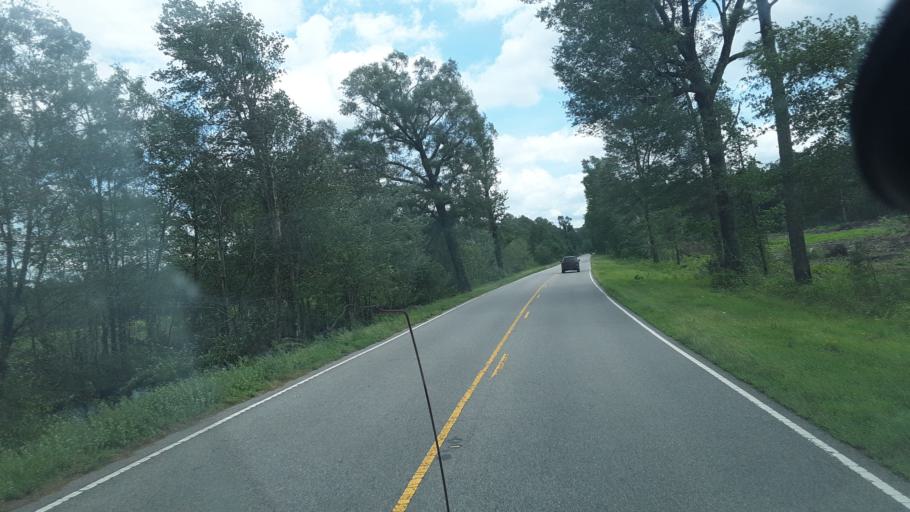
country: US
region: North Carolina
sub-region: Robeson County
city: Fairmont
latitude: 34.3429
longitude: -79.0664
